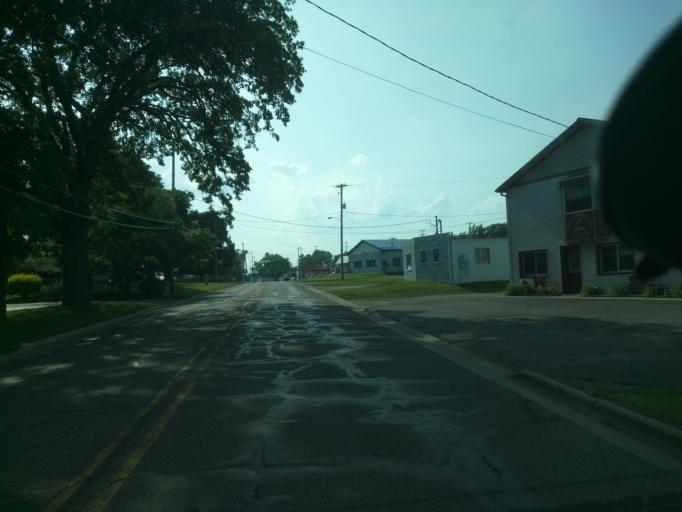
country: US
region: Michigan
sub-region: Jackson County
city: Jackson
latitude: 42.2536
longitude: -84.4351
